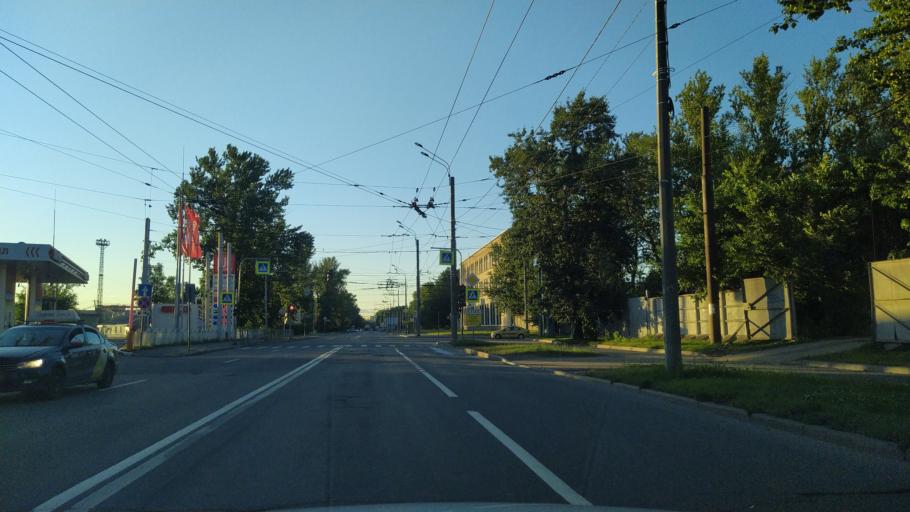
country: RU
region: Leningrad
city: Finlyandskiy
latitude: 59.9645
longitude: 30.3678
